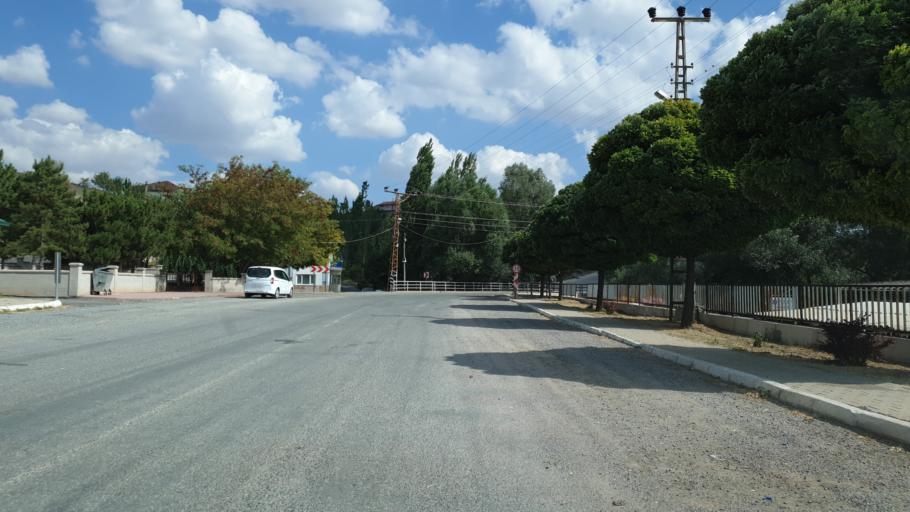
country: TR
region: Kayseri
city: Felahiye
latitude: 39.0944
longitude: 35.5625
